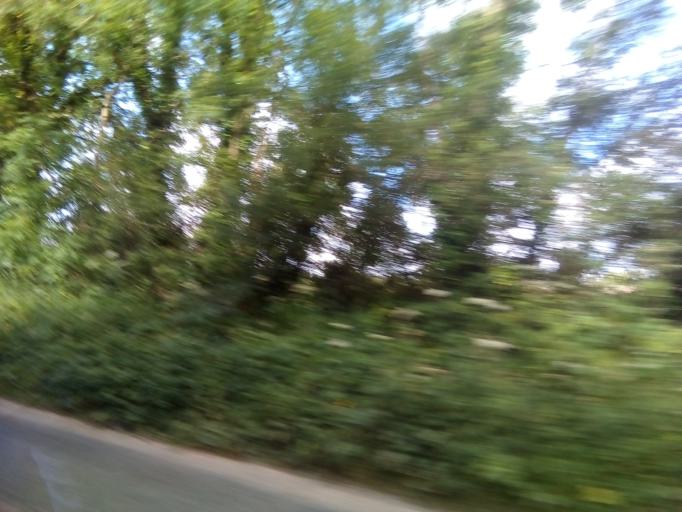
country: IE
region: Leinster
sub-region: Loch Garman
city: Loch Garman
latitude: 52.2720
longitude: -6.5489
